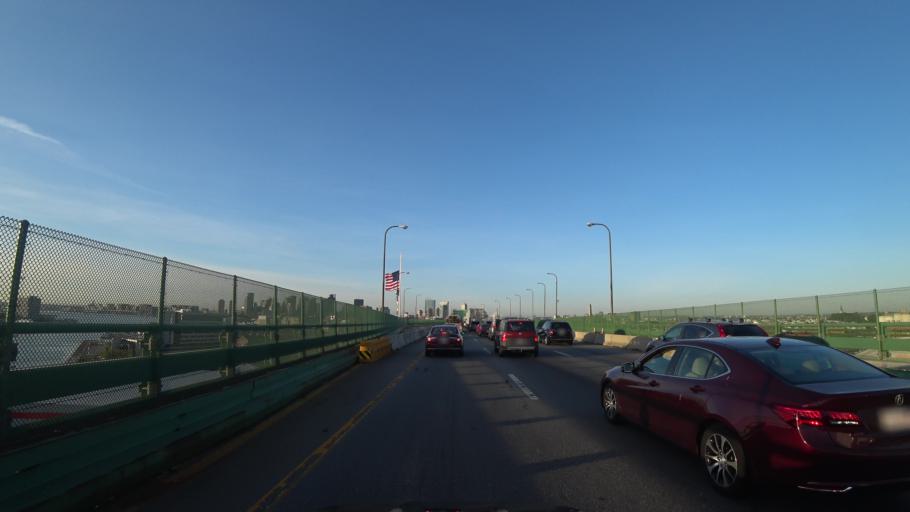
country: US
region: Massachusetts
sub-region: Suffolk County
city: Chelsea
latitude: 42.3829
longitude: -71.0493
